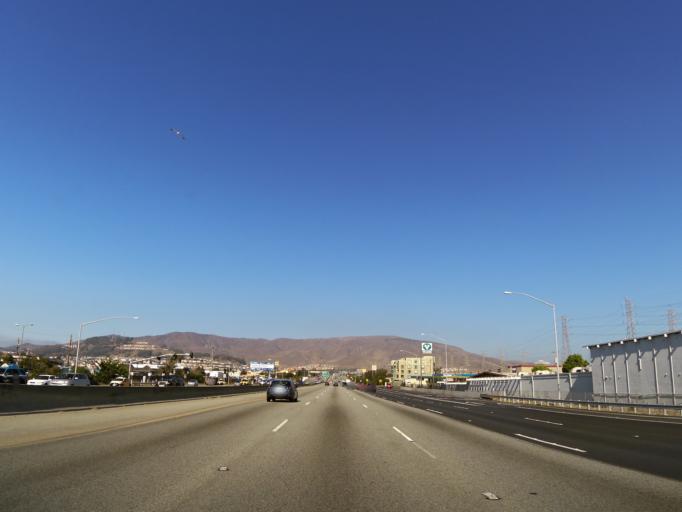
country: US
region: California
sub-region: San Mateo County
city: South San Francisco
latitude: 37.6444
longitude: -122.4061
